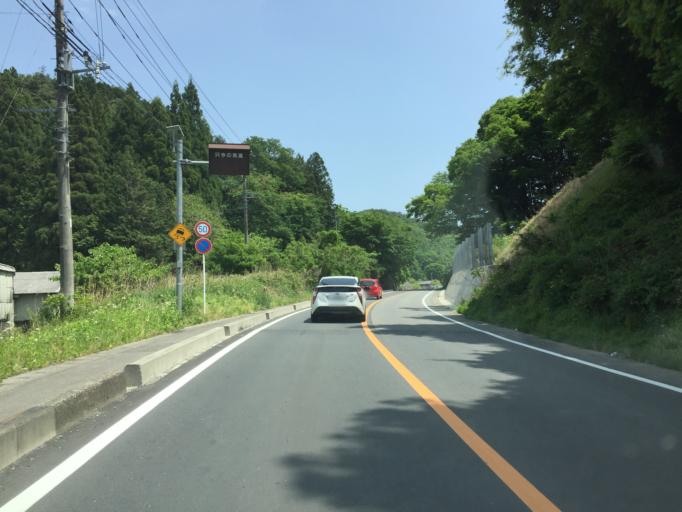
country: JP
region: Fukushima
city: Ishikawa
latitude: 37.1170
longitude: 140.3030
